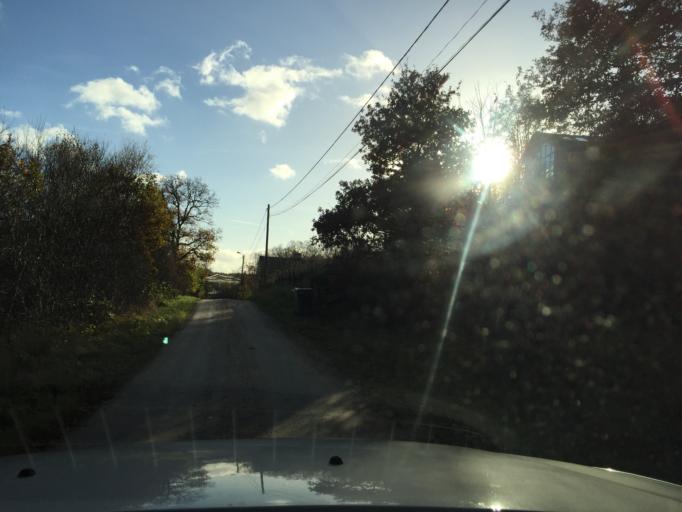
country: SE
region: Skane
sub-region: Hassleholms Kommun
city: Tormestorp
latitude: 56.0725
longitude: 13.7356
